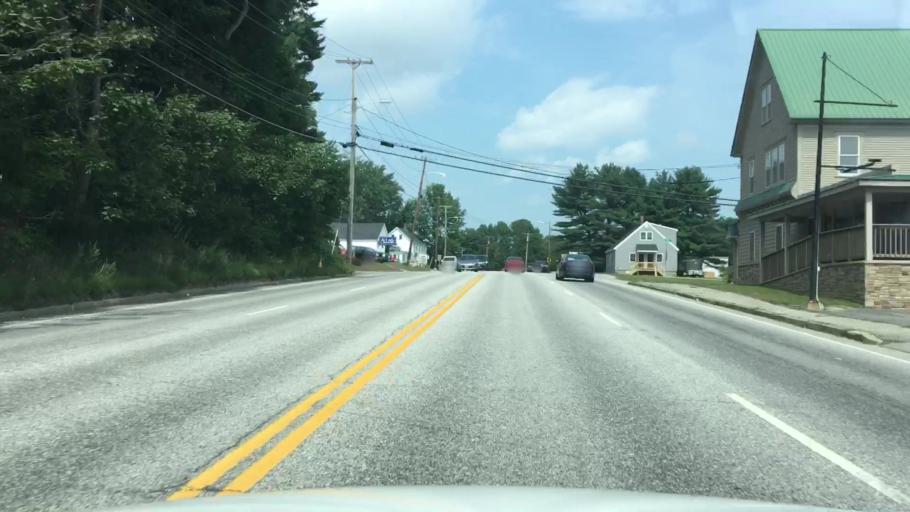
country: US
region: Maine
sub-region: Androscoggin County
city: Lewiston
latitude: 44.1416
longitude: -70.2266
